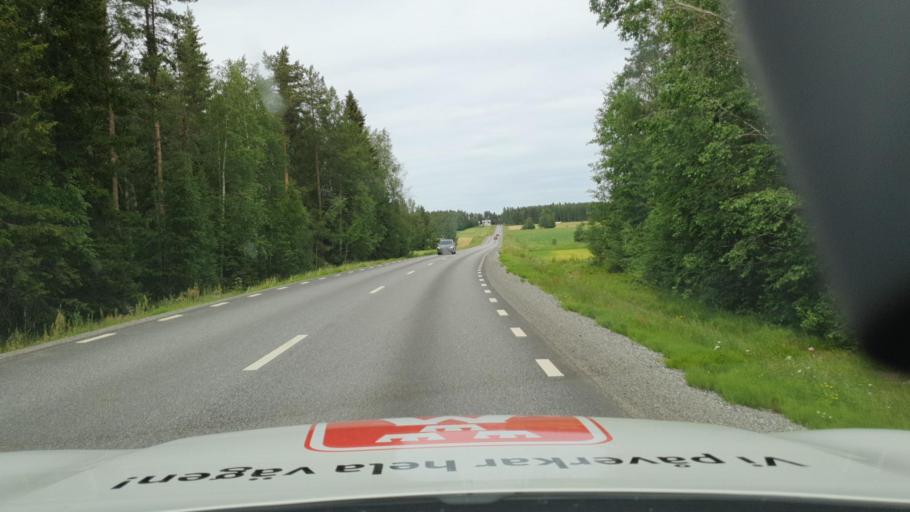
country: SE
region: Vaesterbotten
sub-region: Skelleftea Kommun
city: Burtraesk
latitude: 64.5028
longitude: 20.6255
